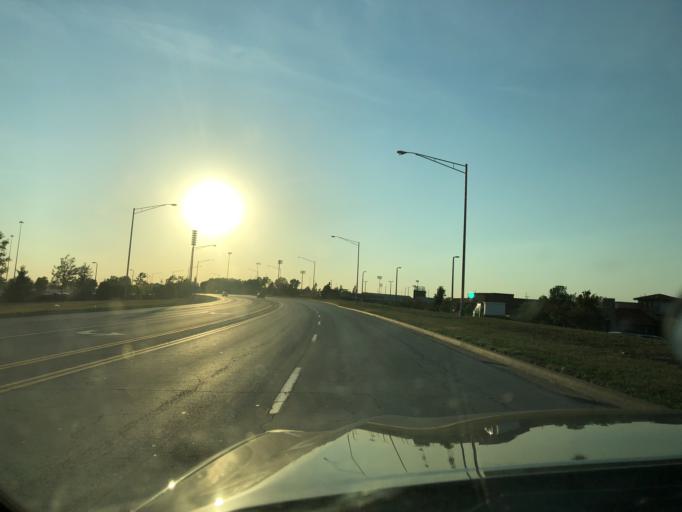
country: US
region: Kansas
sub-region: Wyandotte County
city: Edwardsville
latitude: 39.1224
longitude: -94.8261
